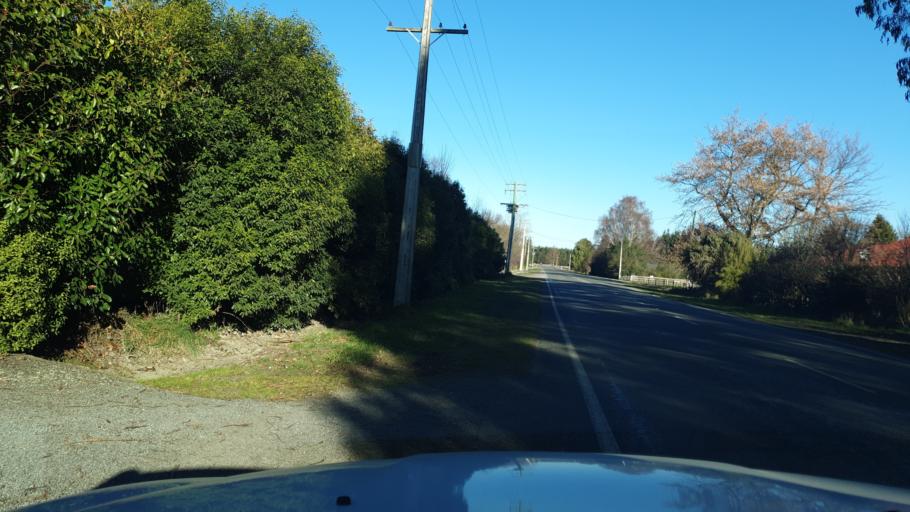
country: NZ
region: Canterbury
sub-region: Timaru District
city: Pleasant Point
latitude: -44.1118
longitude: 171.2452
